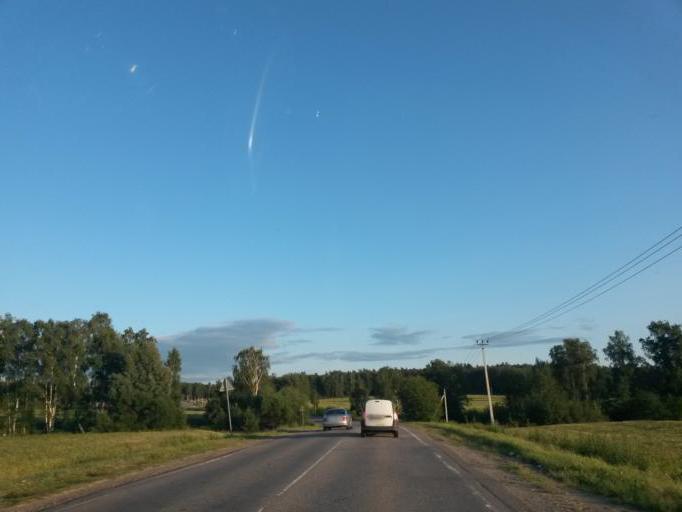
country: RU
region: Moskovskaya
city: Vostryakovo
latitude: 55.3477
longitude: 37.7274
